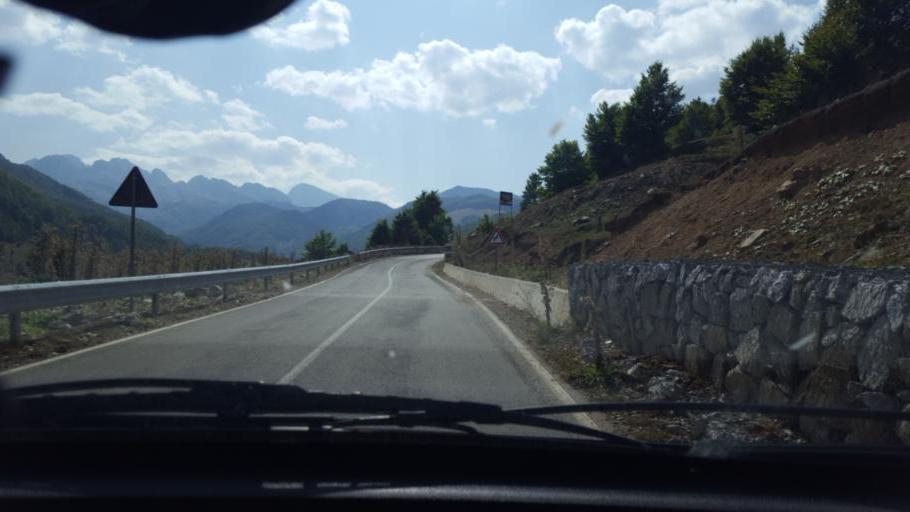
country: AL
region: Kukes
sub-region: Rrethi i Tropojes
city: Valbone
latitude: 42.5487
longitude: 19.7214
